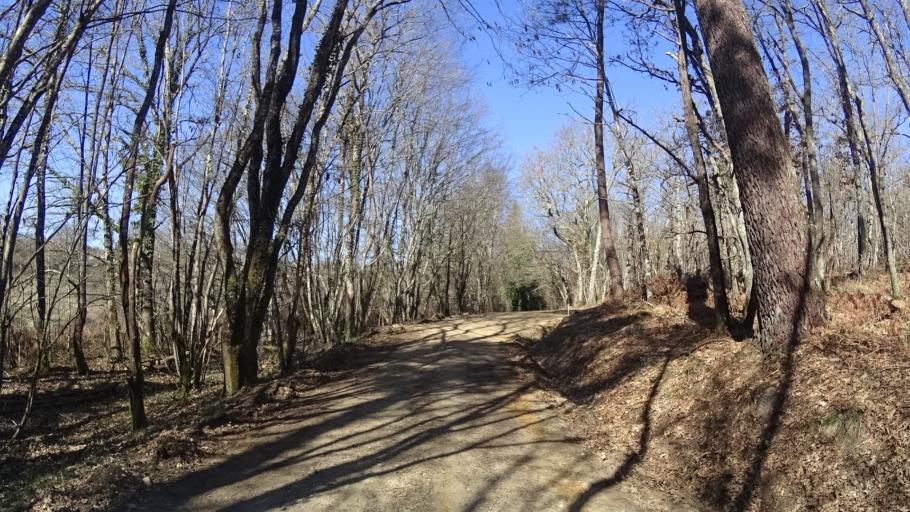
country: FR
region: Aquitaine
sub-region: Departement de la Dordogne
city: Riberac
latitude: 45.1970
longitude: 0.3143
